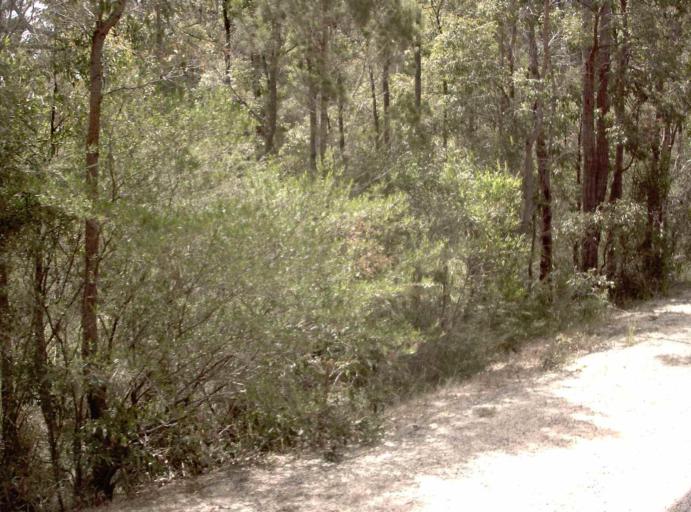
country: AU
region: New South Wales
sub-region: Bega Valley
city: Eden
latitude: -37.4350
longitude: 149.6450
